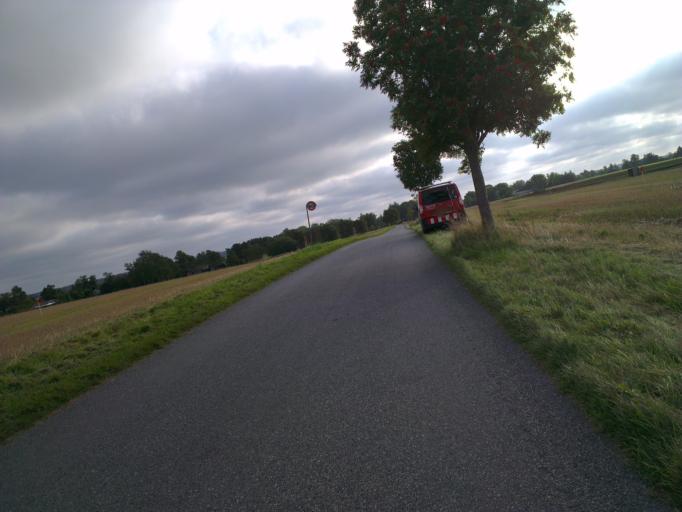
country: DK
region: Capital Region
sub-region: Frederikssund Kommune
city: Frederikssund
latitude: 55.8100
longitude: 12.0297
